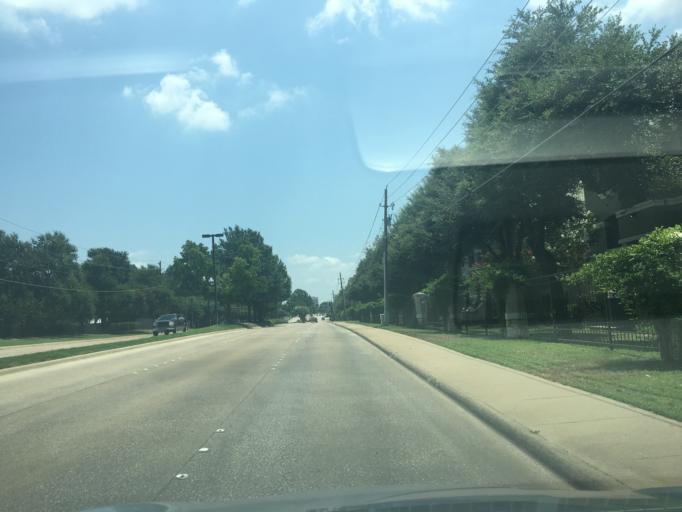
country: US
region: Texas
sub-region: Dallas County
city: Addison
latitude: 32.9398
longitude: -96.8457
